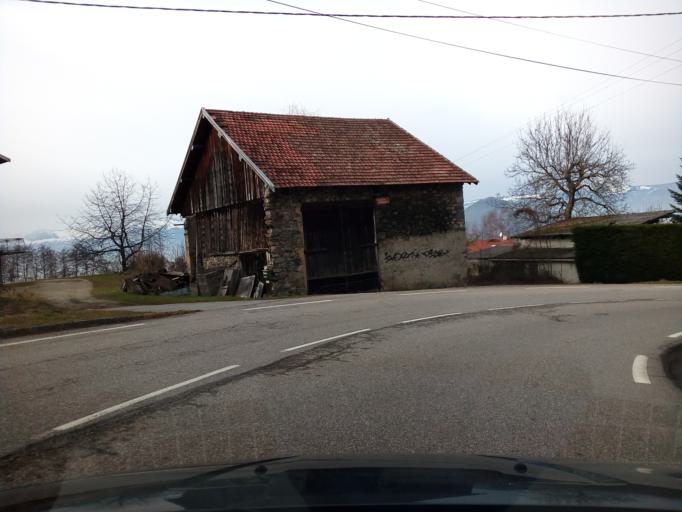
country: FR
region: Rhone-Alpes
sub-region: Departement de l'Isere
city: Revel
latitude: 45.1481
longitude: 5.8533
